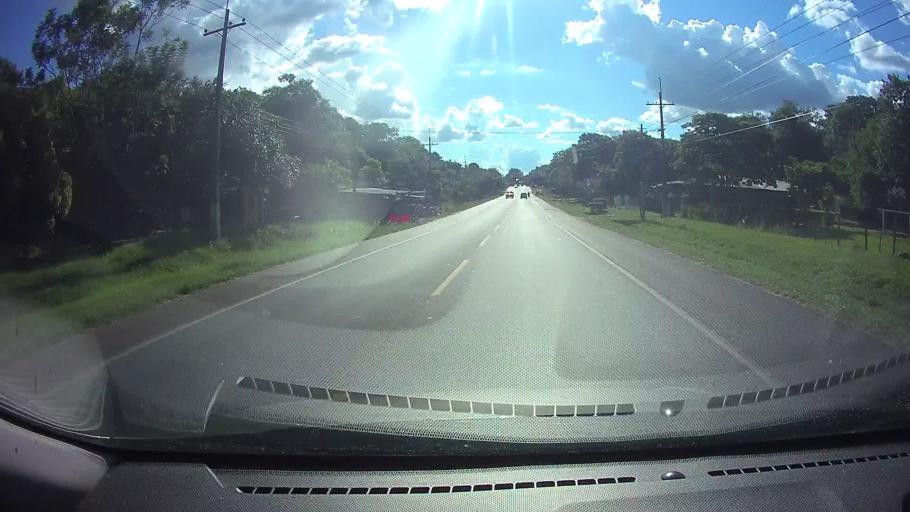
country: PY
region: Cordillera
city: Caacupe
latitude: -25.3884
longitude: -57.1009
